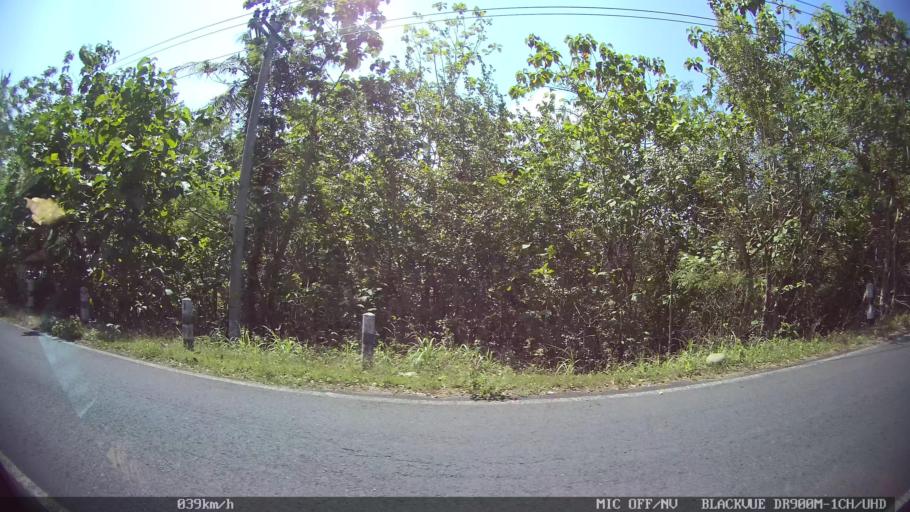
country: ID
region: Daerah Istimewa Yogyakarta
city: Pundong
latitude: -7.9569
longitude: 110.3653
